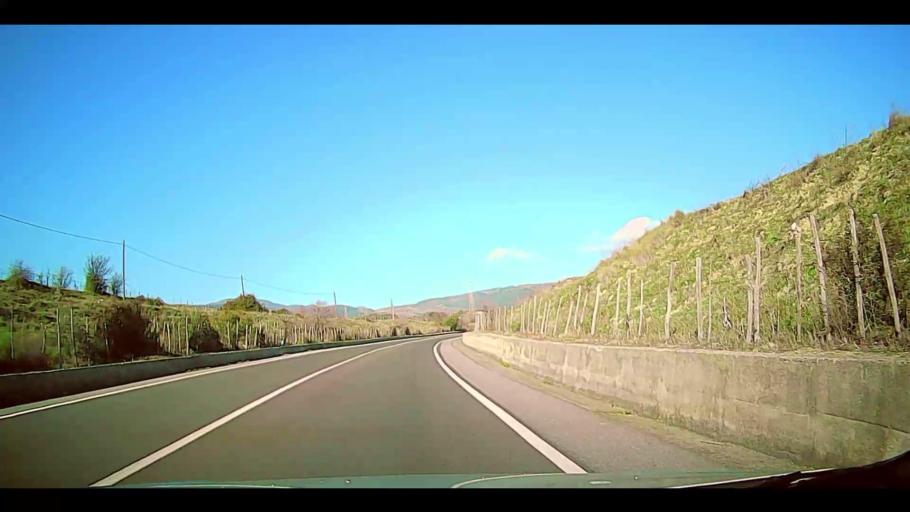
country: IT
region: Calabria
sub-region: Provincia di Crotone
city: Cotronei
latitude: 39.1865
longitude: 16.8190
